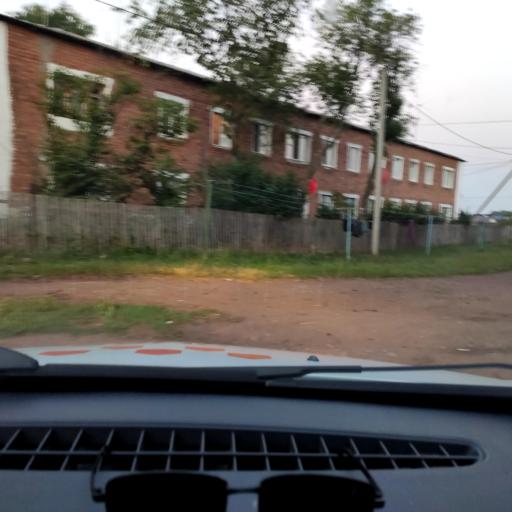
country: RU
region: Bashkortostan
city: Ulukulevo
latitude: 54.3692
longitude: 56.4321
